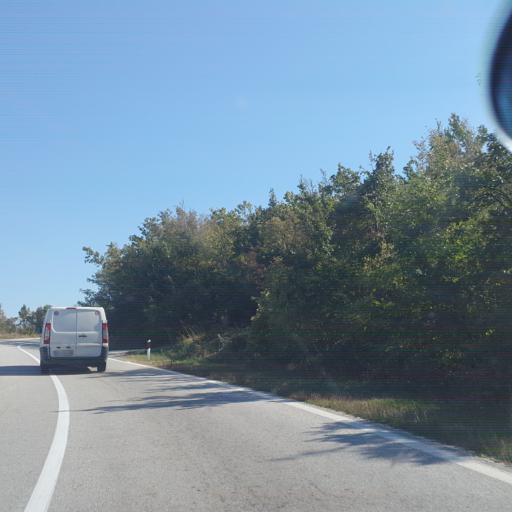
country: RS
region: Central Serbia
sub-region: Zajecarski Okrug
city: Knjazevac
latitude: 43.5179
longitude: 22.2105
